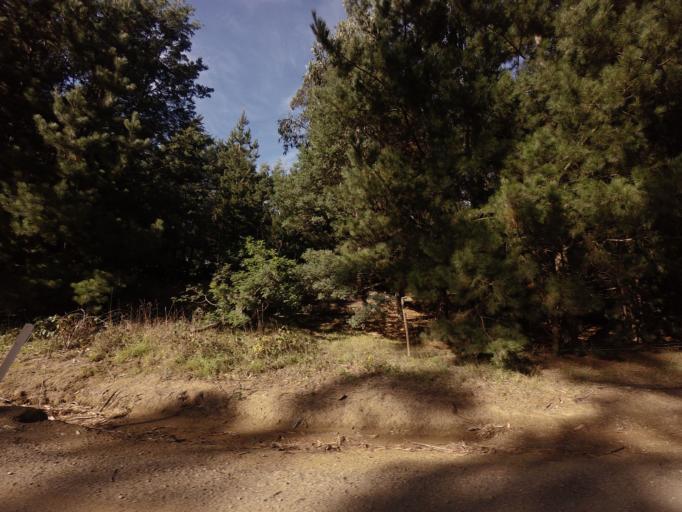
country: AU
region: Tasmania
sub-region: Clarence
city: Sandford
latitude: -43.1475
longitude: 147.7643
